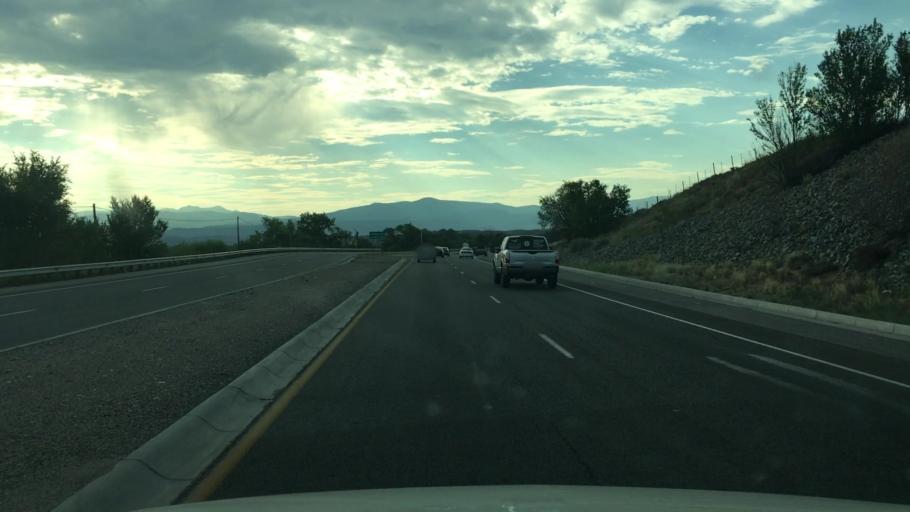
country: US
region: New Mexico
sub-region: Rio Arriba County
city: Espanola
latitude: 35.9862
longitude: -106.0553
